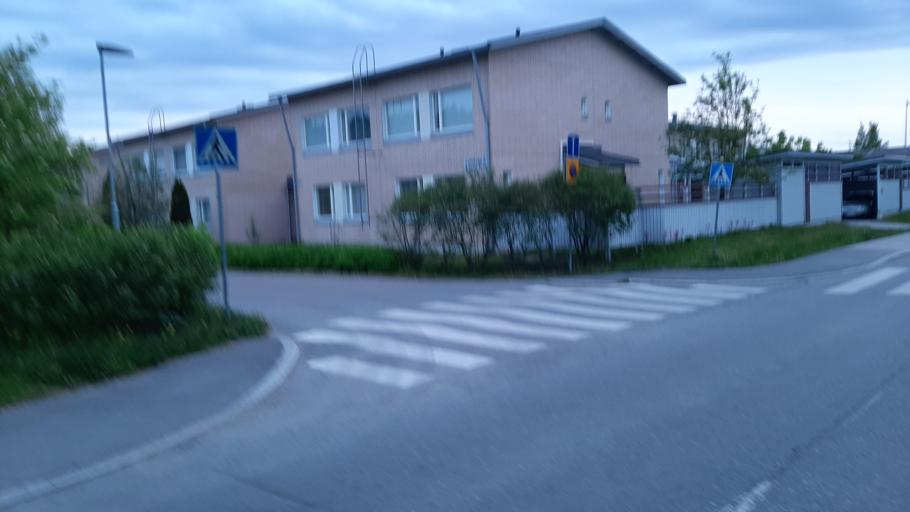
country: FI
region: Pirkanmaa
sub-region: Tampere
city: Tampere
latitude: 61.4736
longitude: 23.8256
